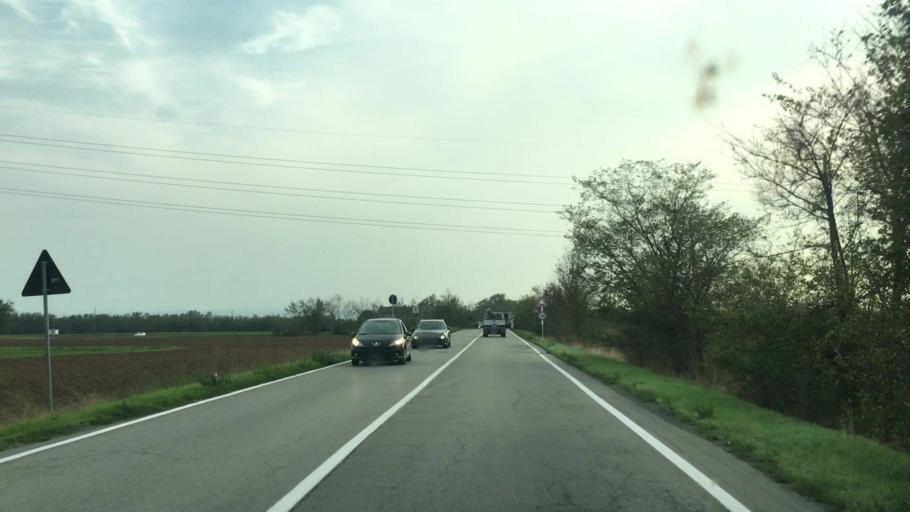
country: IT
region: Emilia-Romagna
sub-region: Provincia di Reggio Emilia
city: Calerno
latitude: 44.7562
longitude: 10.4961
